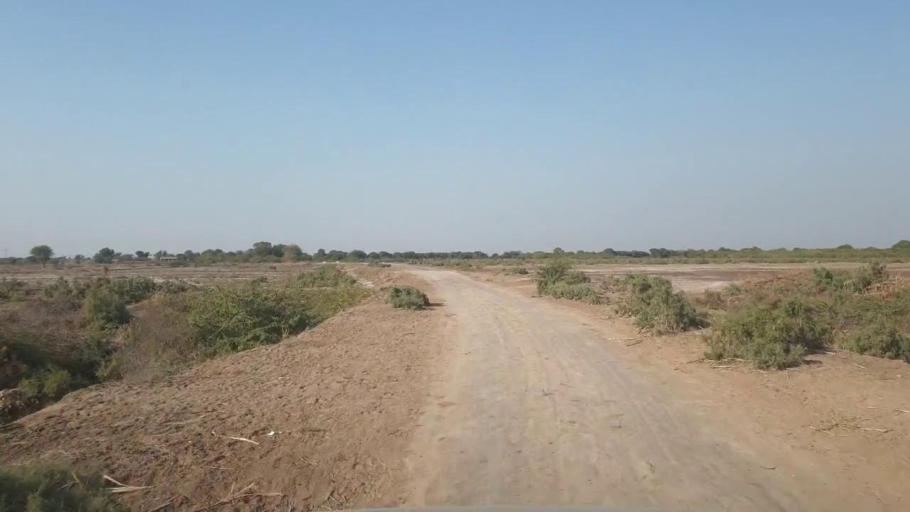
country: PK
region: Sindh
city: Chambar
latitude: 25.2990
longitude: 68.8630
